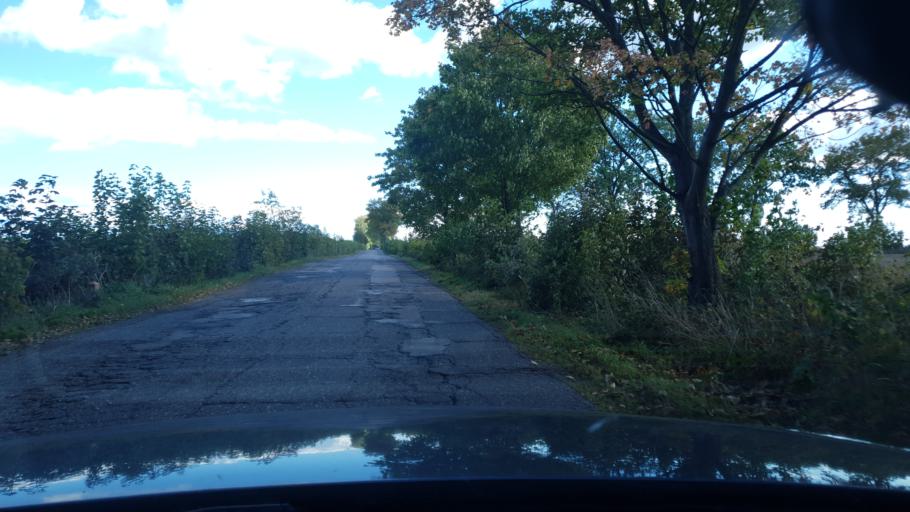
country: PL
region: Pomeranian Voivodeship
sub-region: Powiat pucki
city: Zelistrzewo
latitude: 54.6882
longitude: 18.4303
